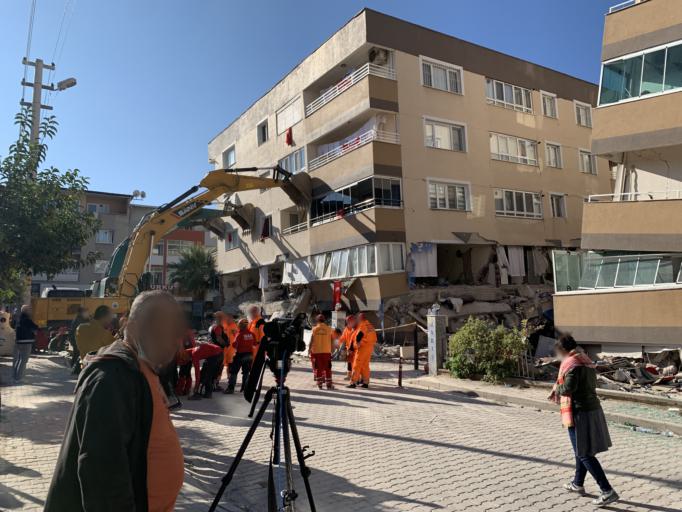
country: TR
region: Izmir
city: Bornova
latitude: 38.4610
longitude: 27.1807
